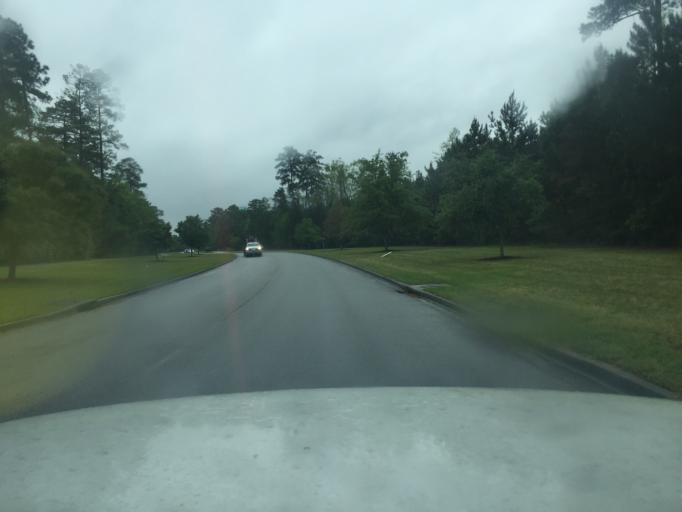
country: US
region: Georgia
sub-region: Chatham County
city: Georgetown
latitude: 32.0407
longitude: -81.2353
